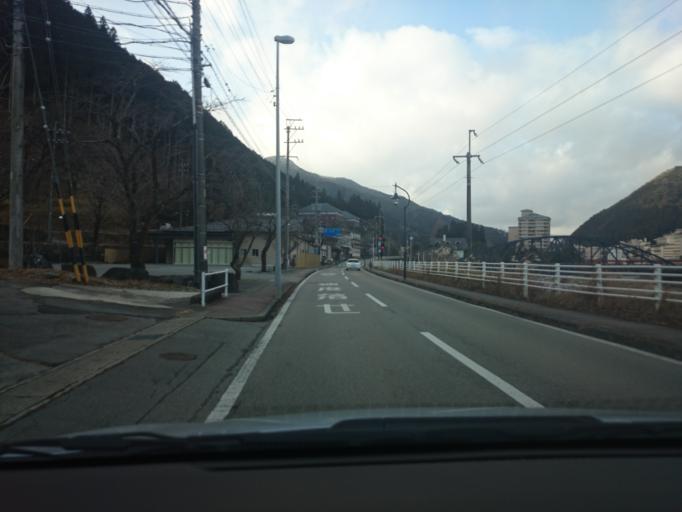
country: JP
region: Gifu
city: Gujo
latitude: 35.8007
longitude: 137.2437
